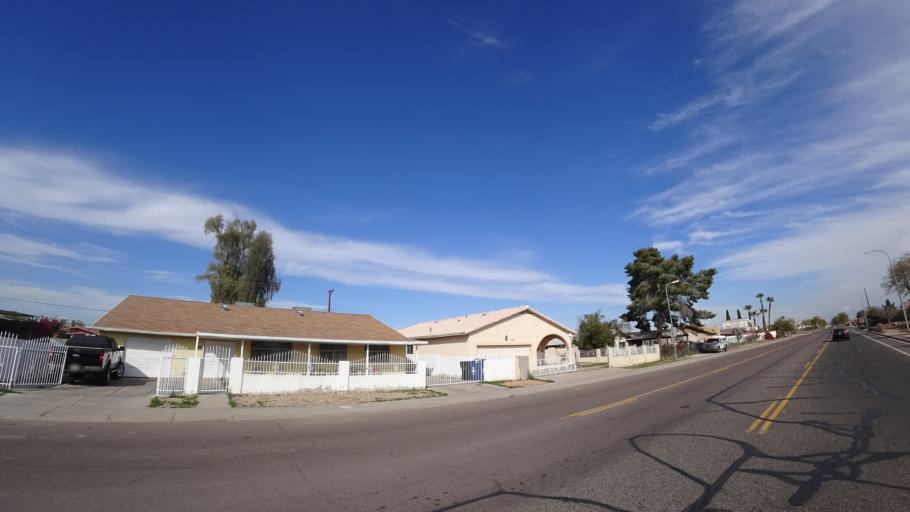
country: US
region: Arizona
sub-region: Maricopa County
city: Tolleson
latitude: 33.4281
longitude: -112.2923
